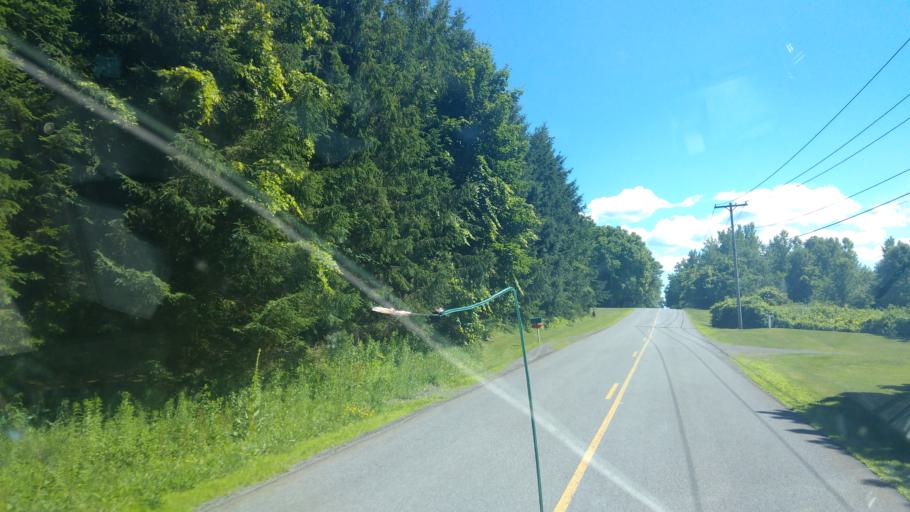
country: US
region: New York
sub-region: Wayne County
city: Sodus
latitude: 43.2347
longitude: -77.0226
